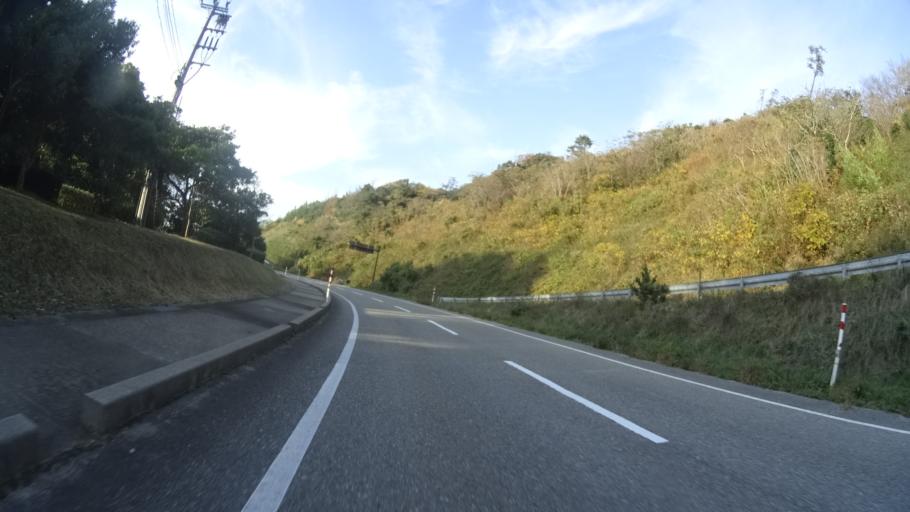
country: JP
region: Ishikawa
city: Hakui
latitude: 37.0993
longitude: 136.7314
